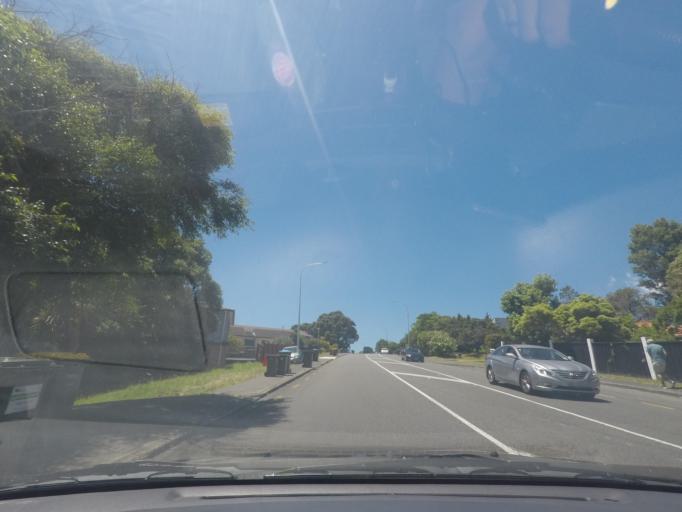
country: NZ
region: Auckland
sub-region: Auckland
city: Auckland
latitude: -36.9278
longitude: 174.7487
